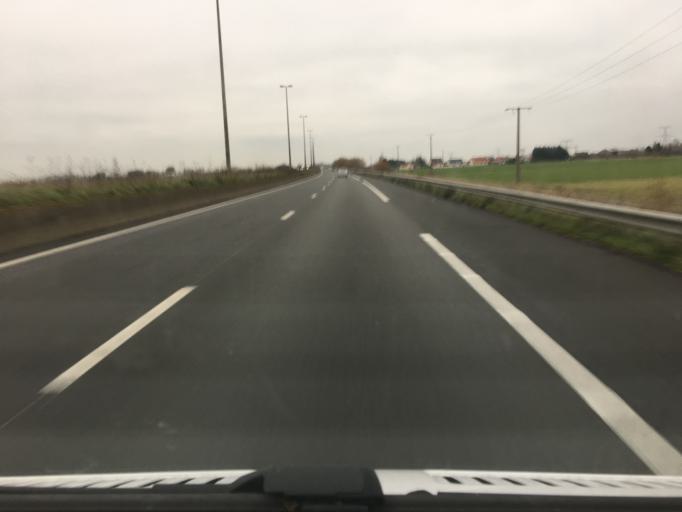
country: FR
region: Nord-Pas-de-Calais
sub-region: Departement du Pas-de-Calais
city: Oye-Plage
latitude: 50.9318
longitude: 2.0231
